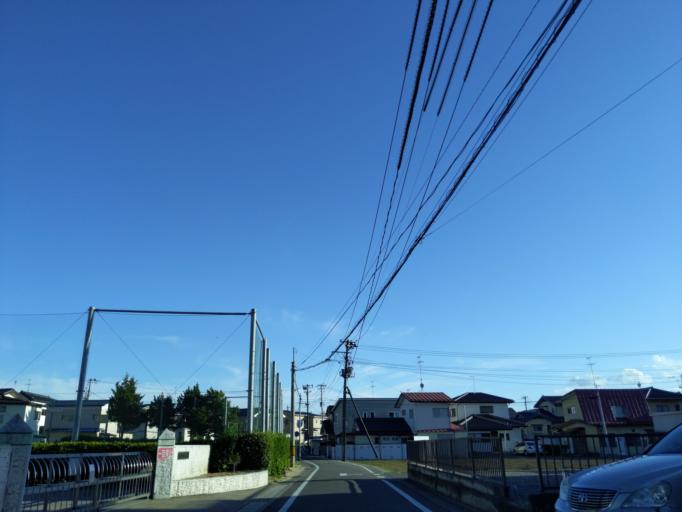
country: JP
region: Fukushima
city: Koriyama
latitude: 37.3915
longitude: 140.4061
